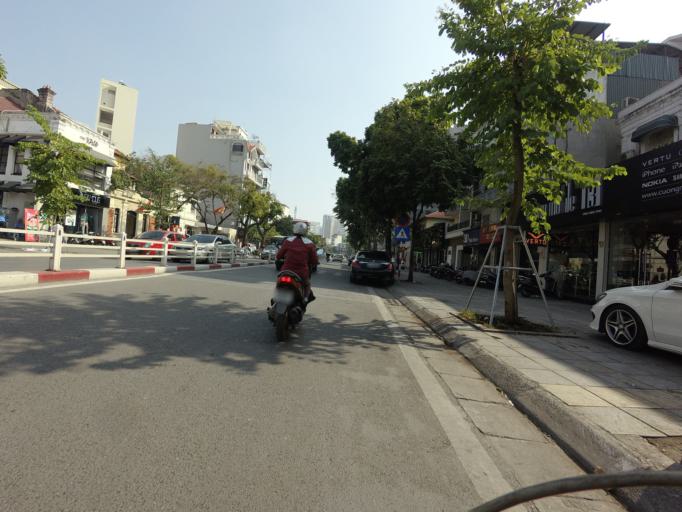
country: VN
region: Ha Noi
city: Hanoi
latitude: 21.0298
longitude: 105.8419
